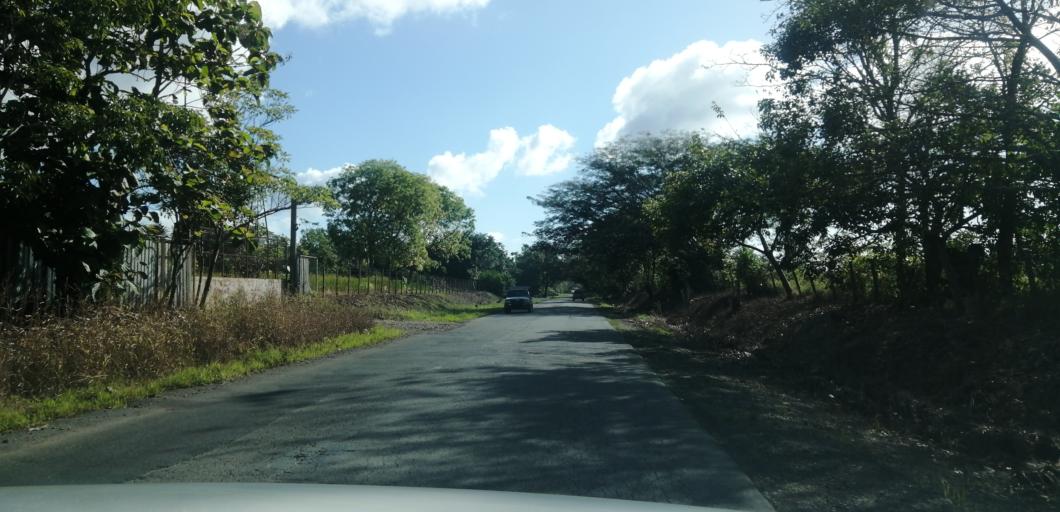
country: PA
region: Panama
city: Canita
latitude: 9.2211
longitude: -78.8833
